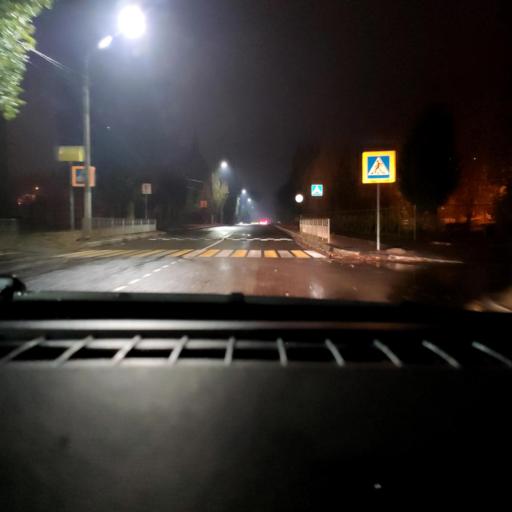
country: RU
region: Voronezj
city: Pridonskoy
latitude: 51.6578
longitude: 39.1105
